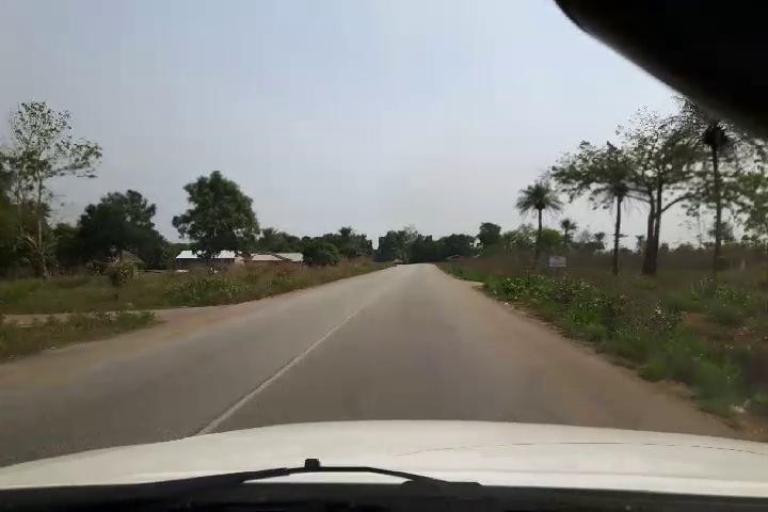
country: SL
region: Southern Province
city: Largo
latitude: 8.3123
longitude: -12.2165
